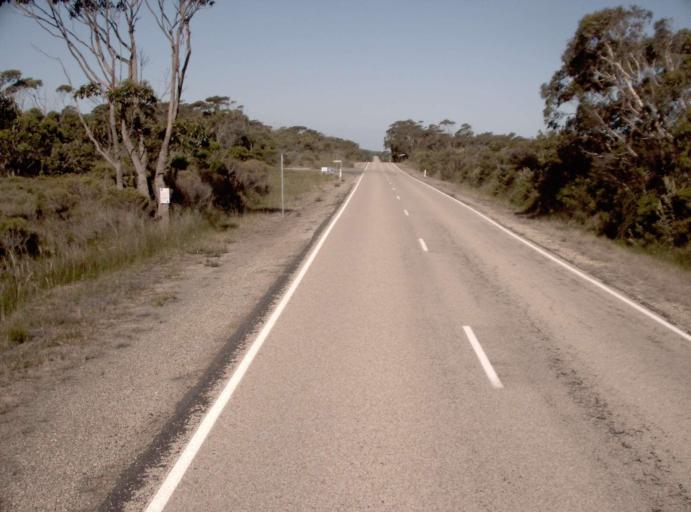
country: AU
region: Victoria
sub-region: East Gippsland
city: Lakes Entrance
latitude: -37.8016
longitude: 148.6368
